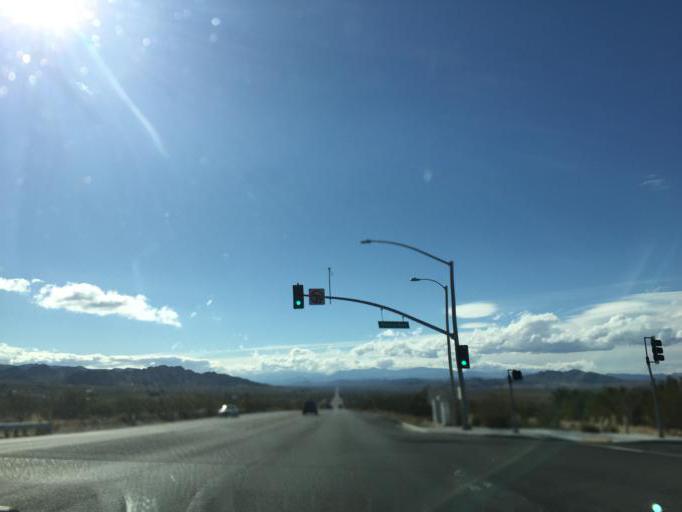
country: US
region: California
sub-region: San Bernardino County
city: Joshua Tree
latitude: 34.1352
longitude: -116.2115
